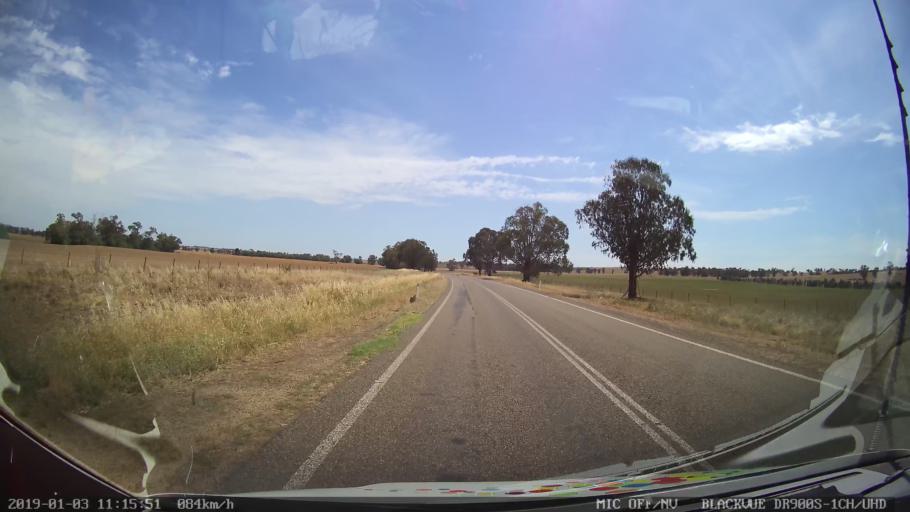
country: AU
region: New South Wales
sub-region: Young
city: Young
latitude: -34.1593
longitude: 148.2680
